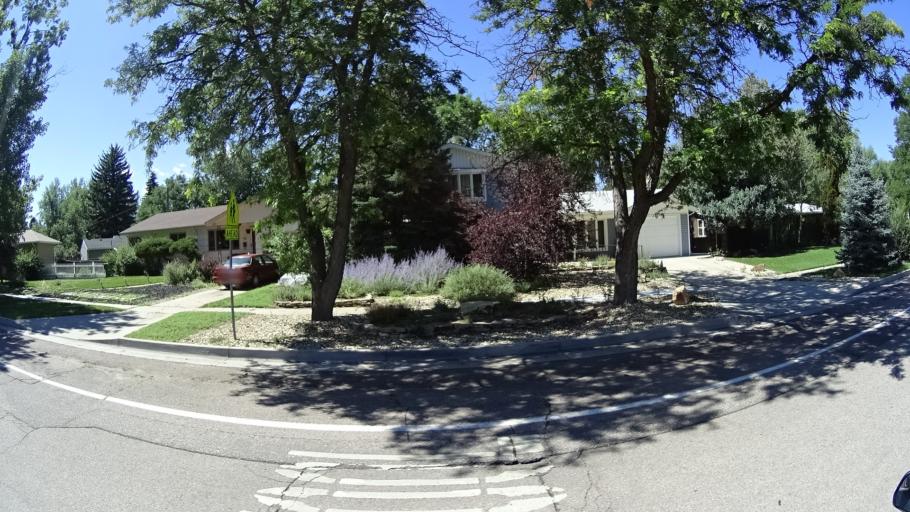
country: US
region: Colorado
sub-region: El Paso County
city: Colorado Springs
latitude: 38.8654
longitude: -104.8051
